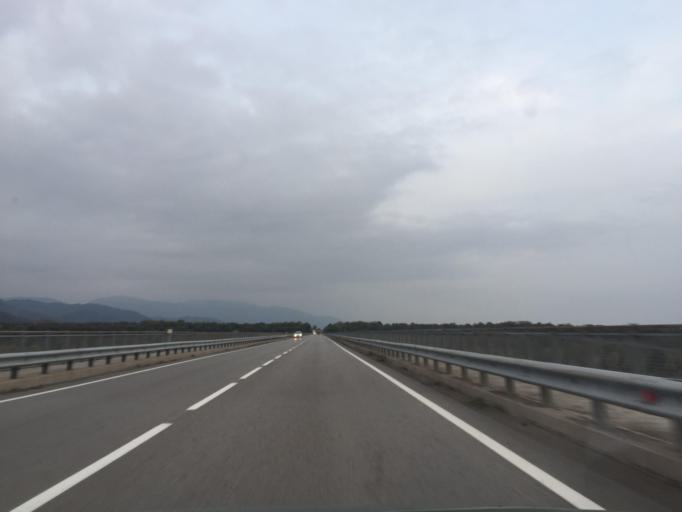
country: IT
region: Friuli Venezia Giulia
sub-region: Provincia di Pordenone
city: Vajont
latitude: 46.1488
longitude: 12.6747
